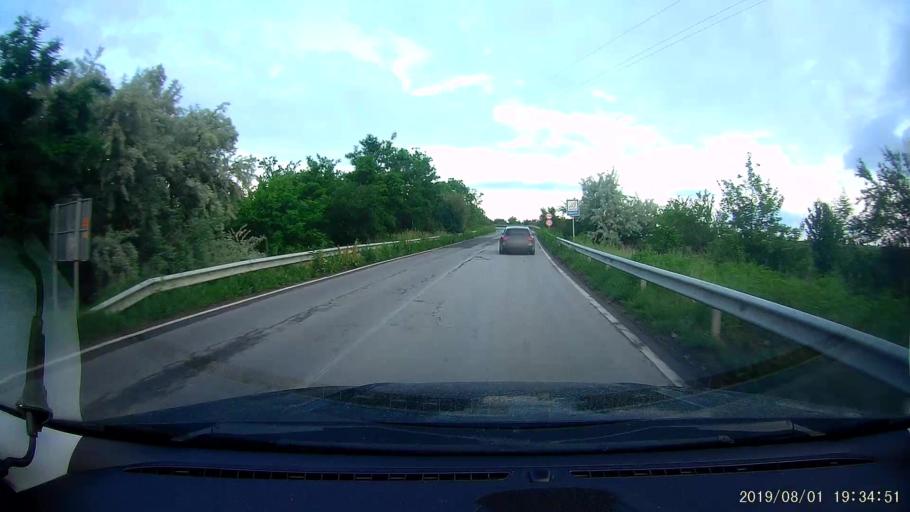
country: BG
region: Burgas
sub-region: Obshtina Sungurlare
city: Sungurlare
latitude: 42.7676
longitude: 26.8788
